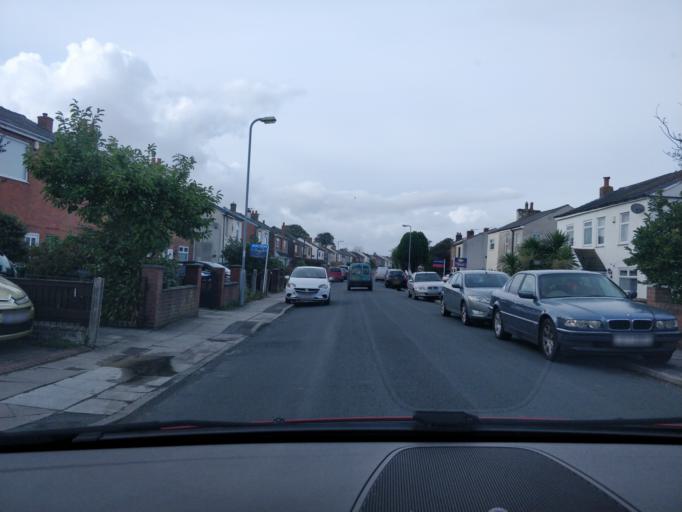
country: GB
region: England
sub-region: Sefton
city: Southport
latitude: 53.6268
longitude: -3.0038
